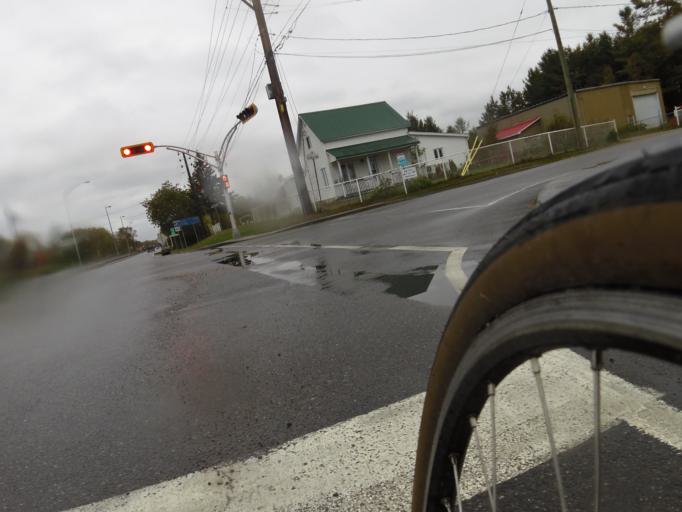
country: CA
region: Quebec
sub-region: Outaouais
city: Fort-Coulonge
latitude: 45.8499
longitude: -76.7274
